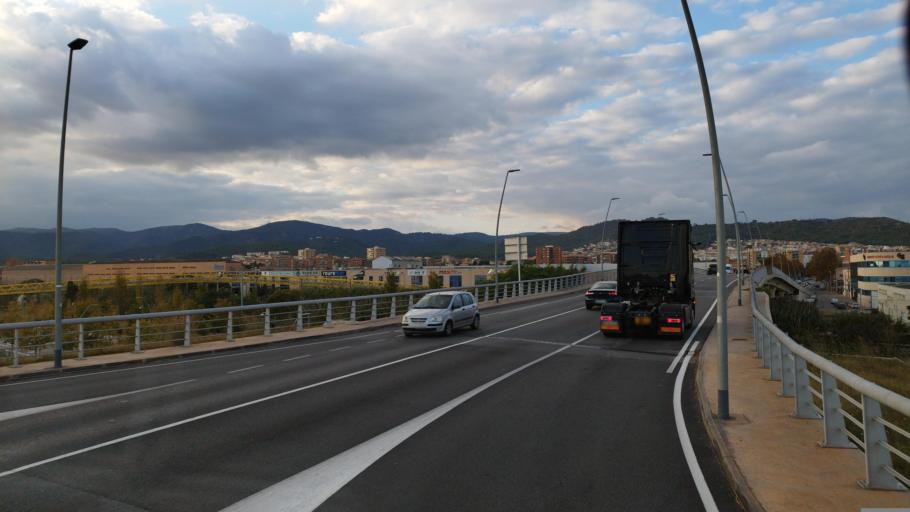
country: ES
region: Catalonia
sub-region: Provincia de Barcelona
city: Viladecans
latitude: 41.3064
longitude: 2.0219
